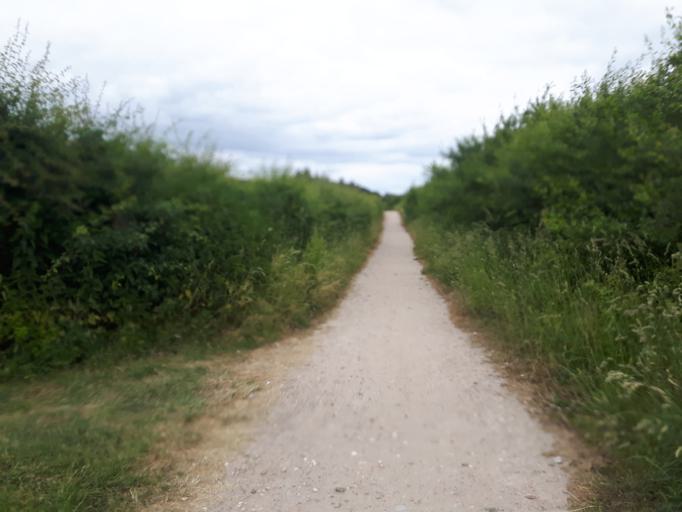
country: DE
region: Schleswig-Holstein
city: Schashagen
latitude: 54.1214
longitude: 10.9282
